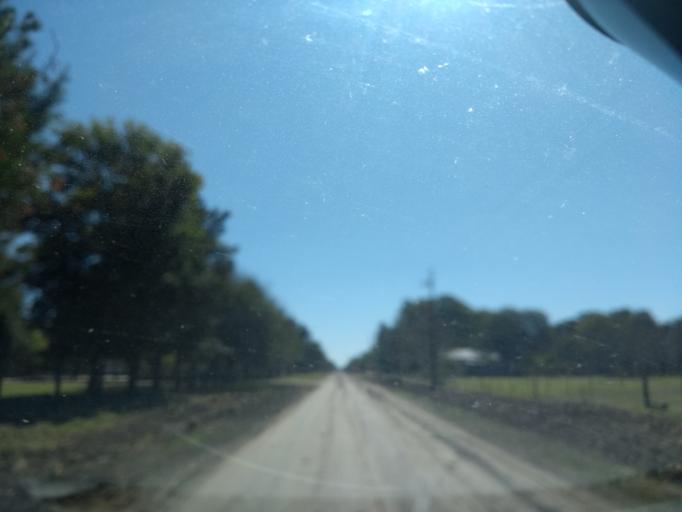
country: AR
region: Chaco
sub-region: Departamento de Quitilipi
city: Quitilipi
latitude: -26.7567
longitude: -60.2431
